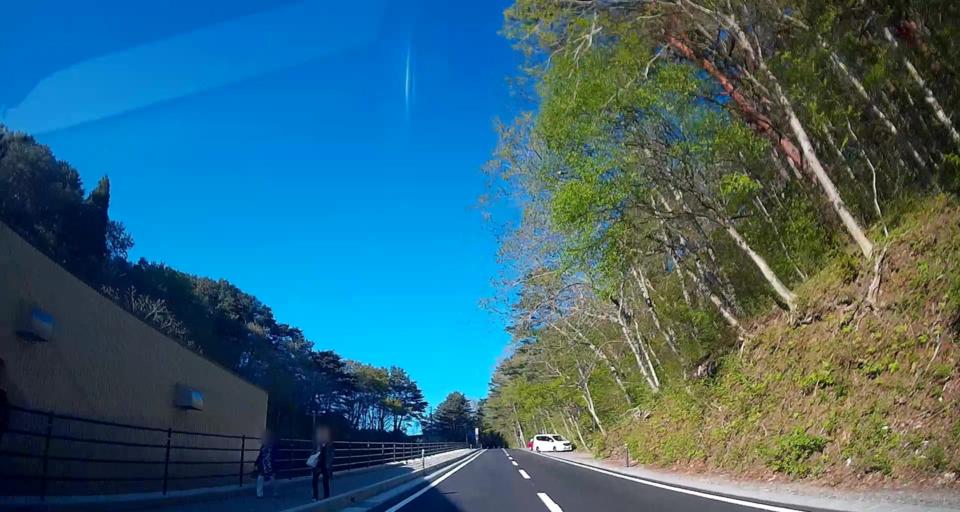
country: JP
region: Iwate
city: Miyako
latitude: 39.6449
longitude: 141.9763
